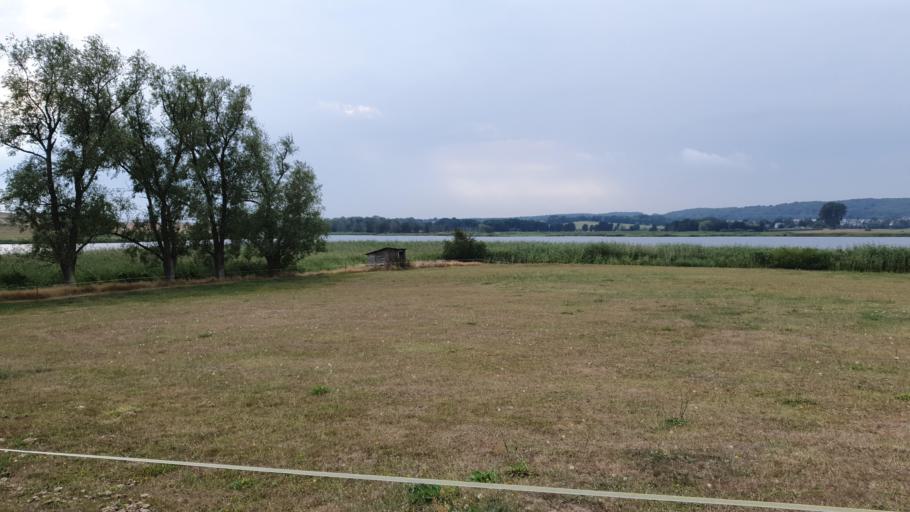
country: DE
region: Mecklenburg-Vorpommern
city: Ostseebad Sellin
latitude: 54.3595
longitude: 13.6535
